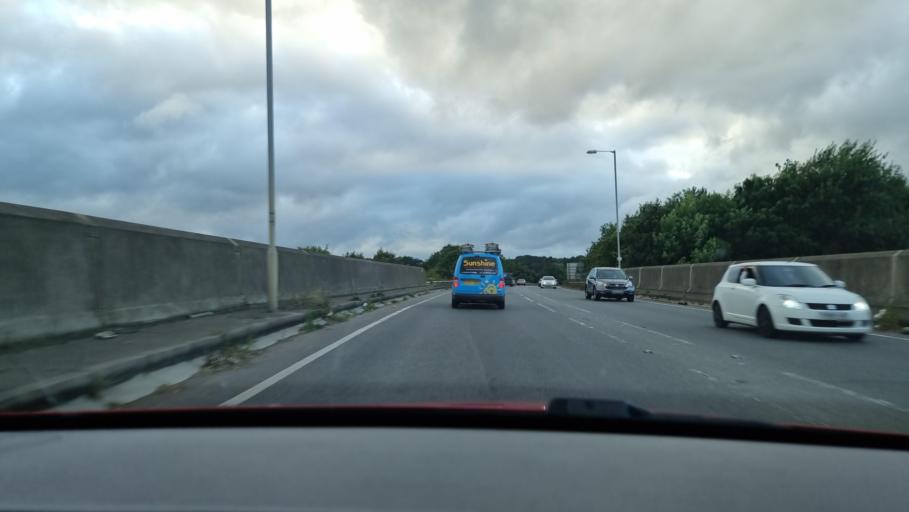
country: GB
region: England
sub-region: Central Bedfordshire
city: Leighton Buzzard
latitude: 51.9008
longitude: -0.6766
